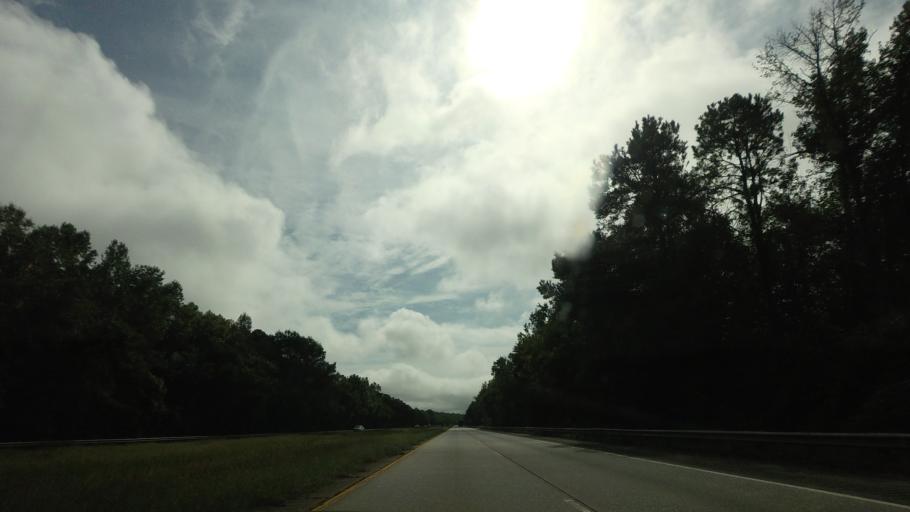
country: US
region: Georgia
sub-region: Bibb County
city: Macon
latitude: 32.8183
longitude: -83.5871
